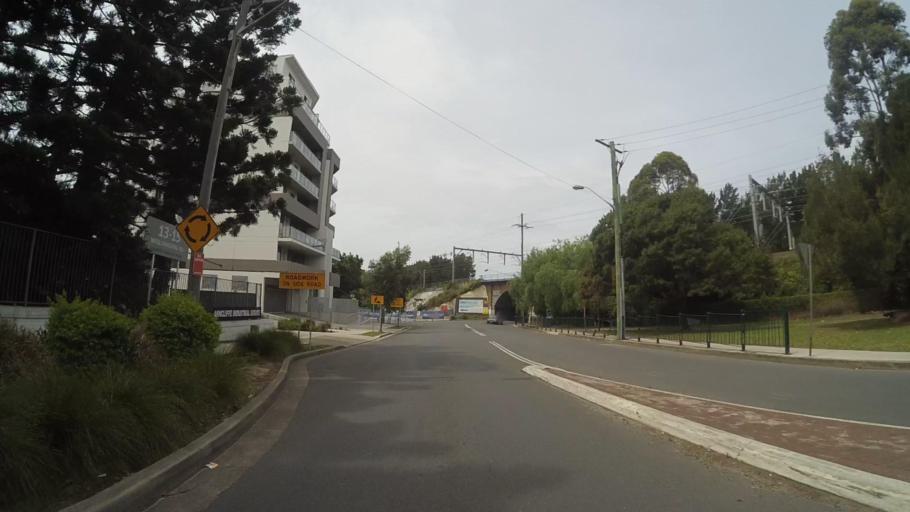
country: AU
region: New South Wales
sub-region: Rockdale
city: Arncliffe
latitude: -33.9340
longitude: 151.1479
